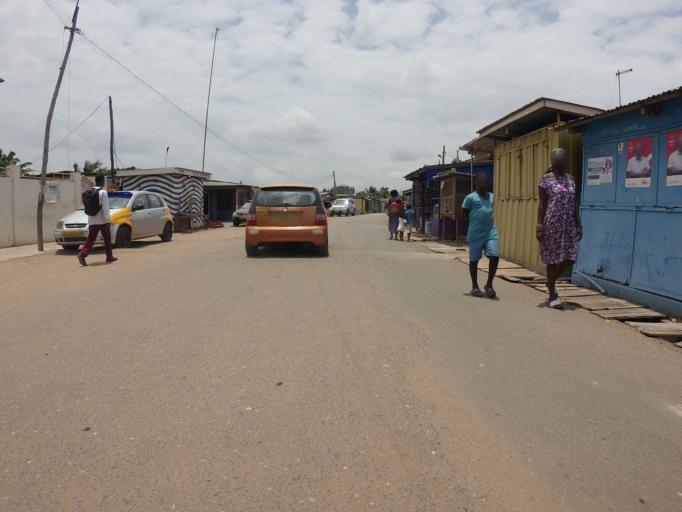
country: GH
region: Greater Accra
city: Nungua
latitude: 5.6003
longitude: -0.0833
